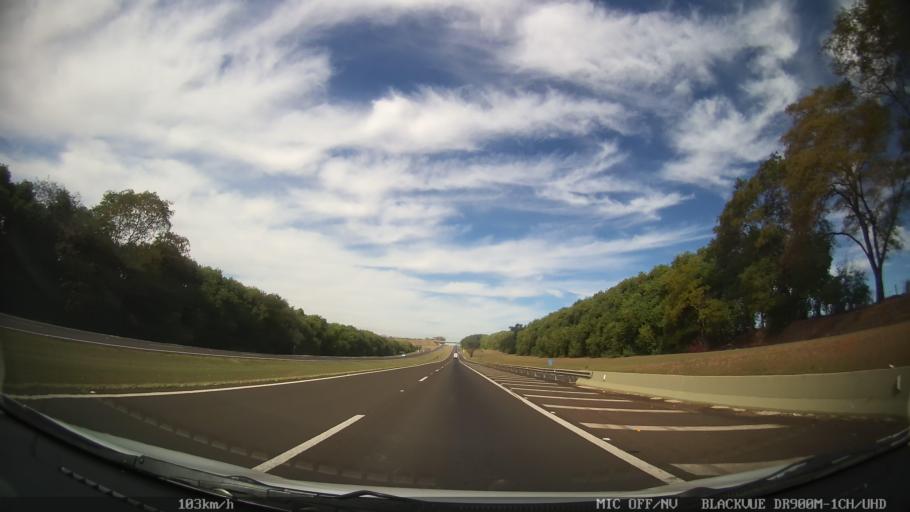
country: BR
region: Sao Paulo
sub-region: Matao
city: Matao
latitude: -21.6358
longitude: -48.3992
